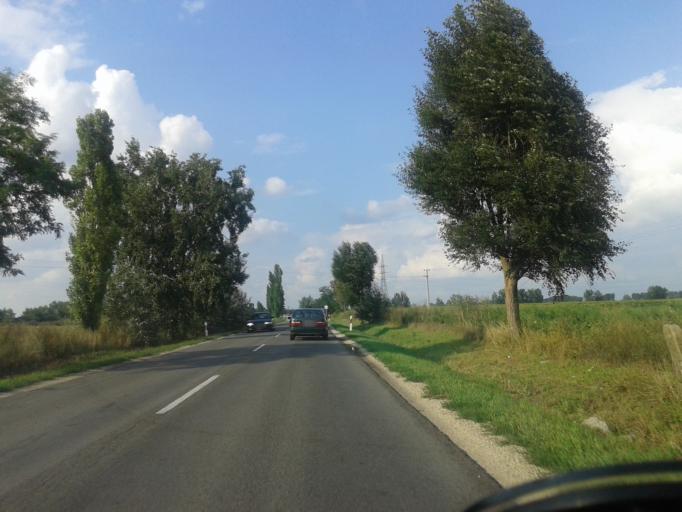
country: HU
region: Pest
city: Kiskunlachaza
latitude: 47.1495
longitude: 18.9978
